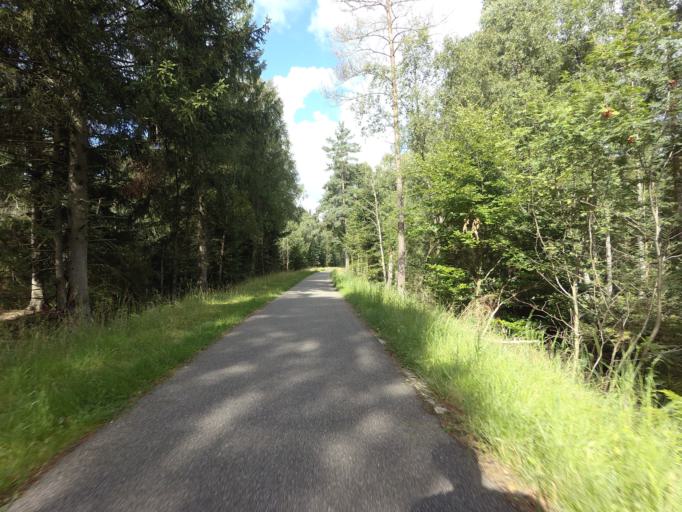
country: DK
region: Central Jutland
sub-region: Silkeborg Kommune
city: Silkeborg
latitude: 56.1658
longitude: 9.5902
